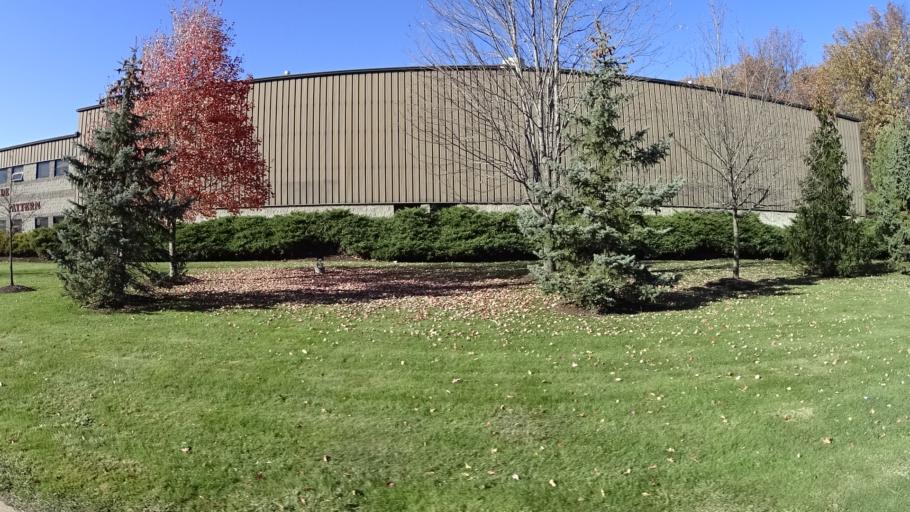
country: US
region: Ohio
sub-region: Lorain County
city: Elyria
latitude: 41.3693
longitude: -82.0708
